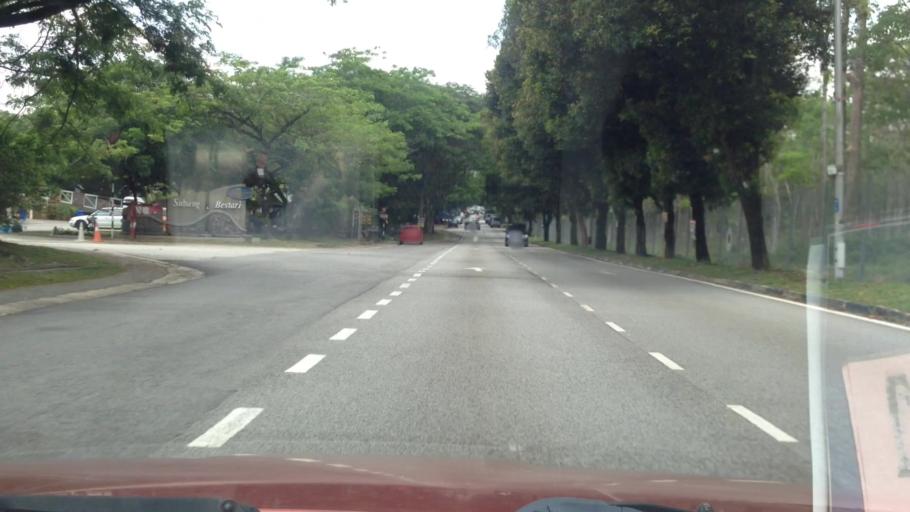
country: MY
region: Selangor
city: Kampung Baru Subang
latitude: 3.1691
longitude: 101.5509
